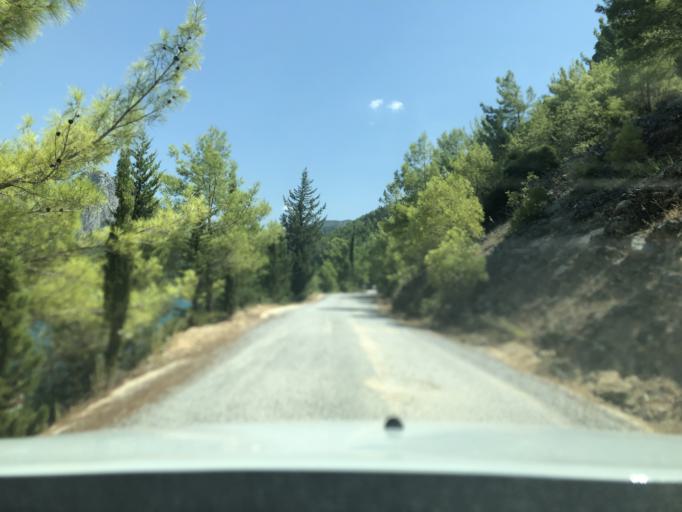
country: TR
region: Antalya
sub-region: Manavgat
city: Manavgat
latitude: 36.9081
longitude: 31.5538
